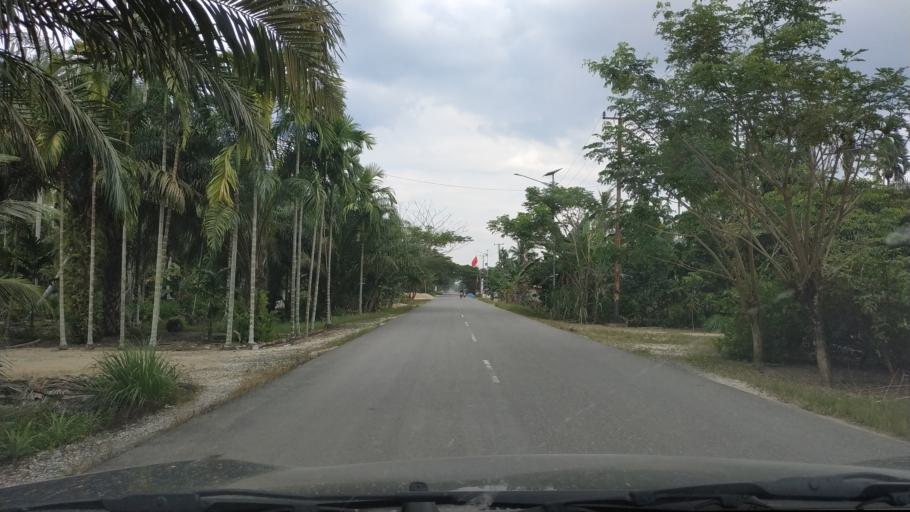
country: ID
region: Riau
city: Sungaisalak
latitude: -0.5675
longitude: 102.9696
